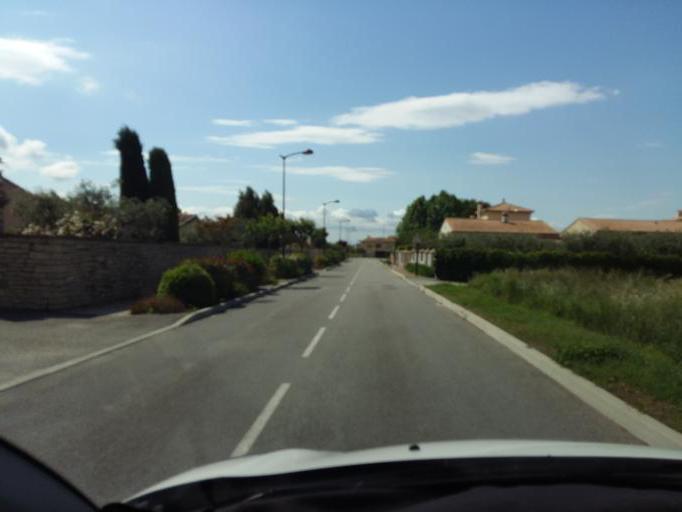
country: FR
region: Provence-Alpes-Cote d'Azur
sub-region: Departement du Vaucluse
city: Taillades
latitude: 43.8424
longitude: 5.0870
